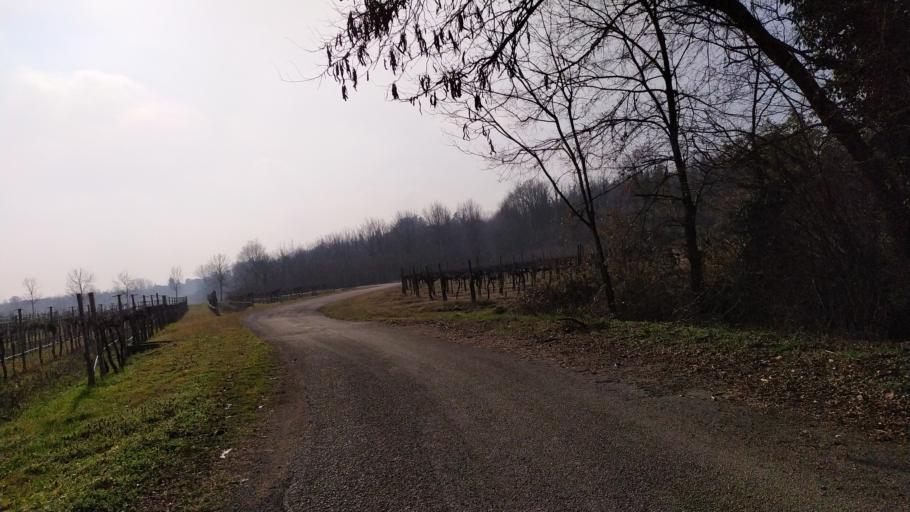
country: IT
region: Veneto
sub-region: Provincia di Treviso
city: Colle Umberto
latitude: 45.9360
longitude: 12.3479
